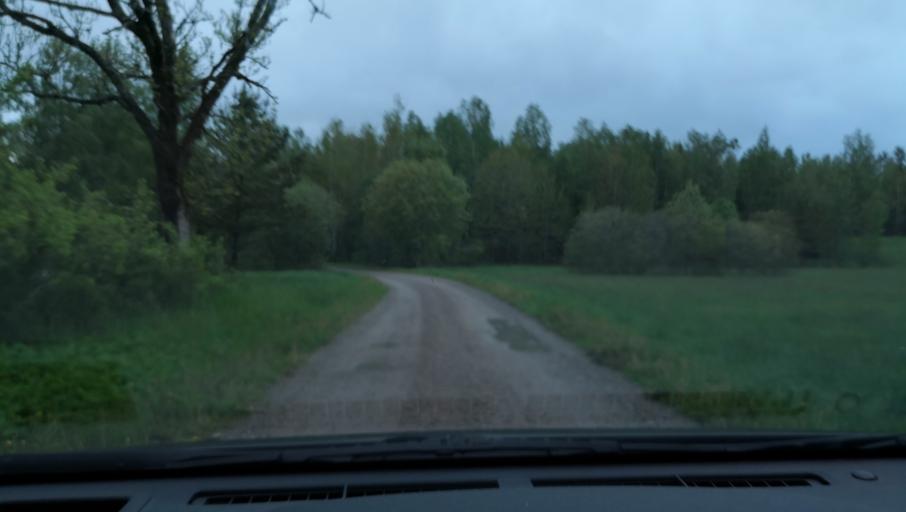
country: SE
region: Uppsala
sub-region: Heby Kommun
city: OEstervala
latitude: 59.9920
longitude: 17.2521
